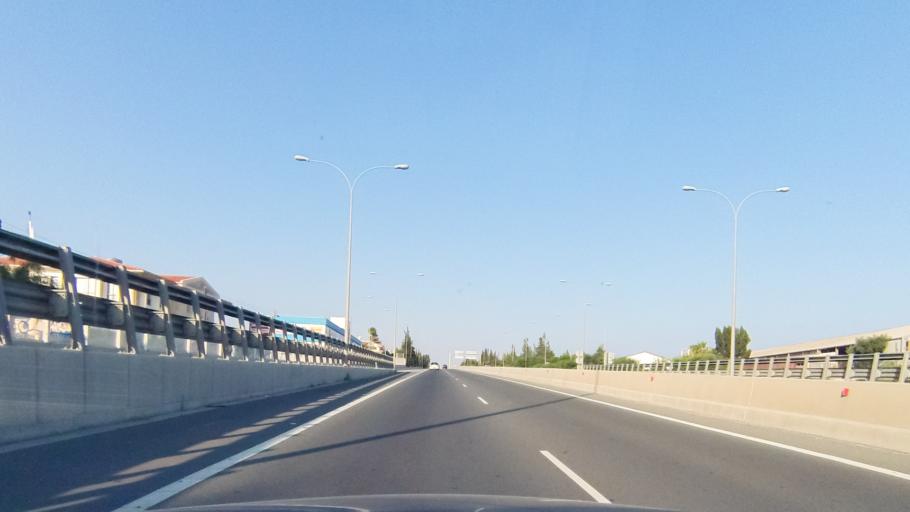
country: CY
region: Limassol
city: Limassol
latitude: 34.7076
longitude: 33.0632
